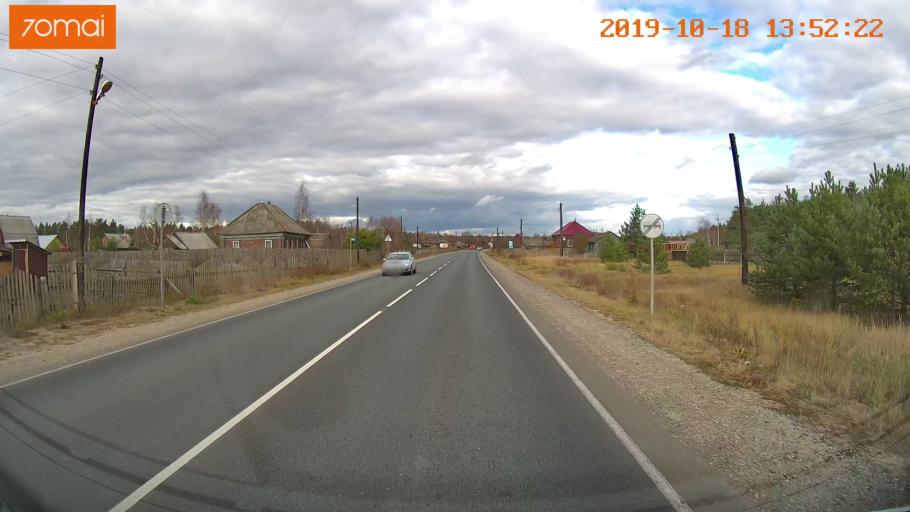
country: RU
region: Moskovskaya
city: Radovitskiy
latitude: 55.0293
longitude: 39.9676
